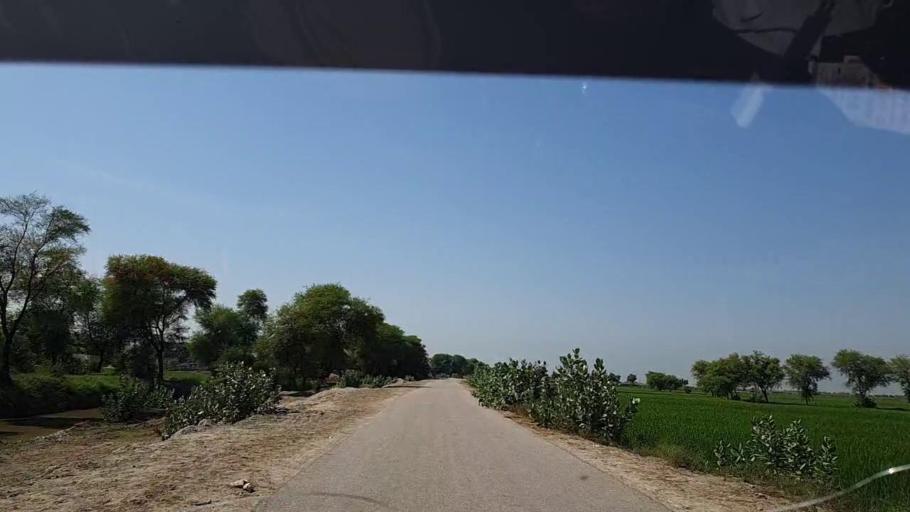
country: PK
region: Sindh
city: Kandhkot
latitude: 28.3048
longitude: 69.1119
